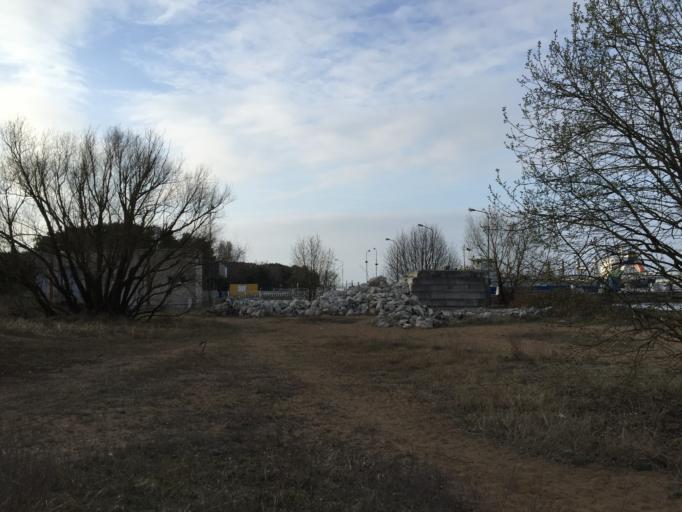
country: LT
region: Klaipedos apskritis
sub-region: Klaipeda
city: Klaipeda
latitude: 55.6848
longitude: 21.1311
